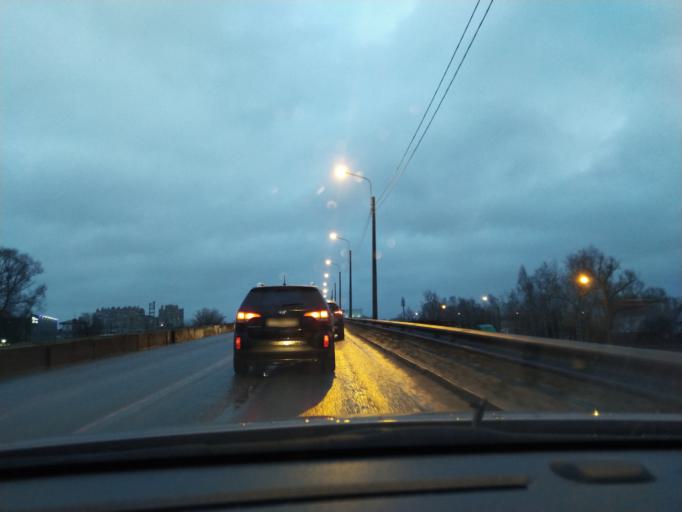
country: RU
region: St.-Petersburg
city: Uritsk
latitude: 59.8207
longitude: 30.1815
